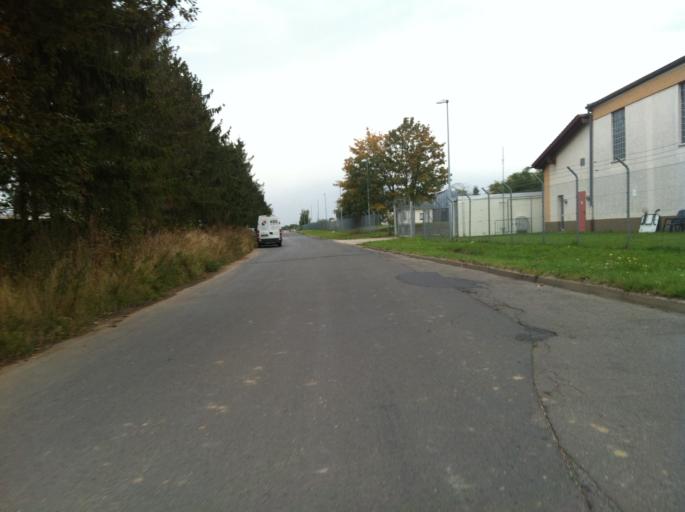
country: DE
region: Rheinland-Pfalz
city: Wackernheim
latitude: 49.9677
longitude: 8.1198
